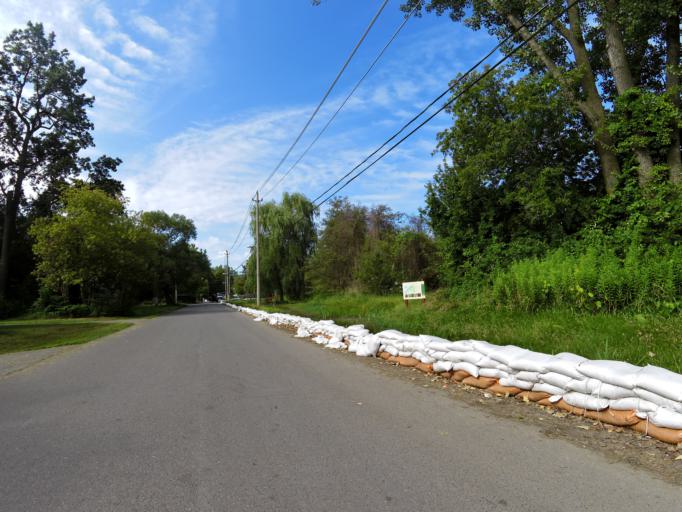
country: CA
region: Ontario
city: Toronto
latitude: 43.6284
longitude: -79.3565
